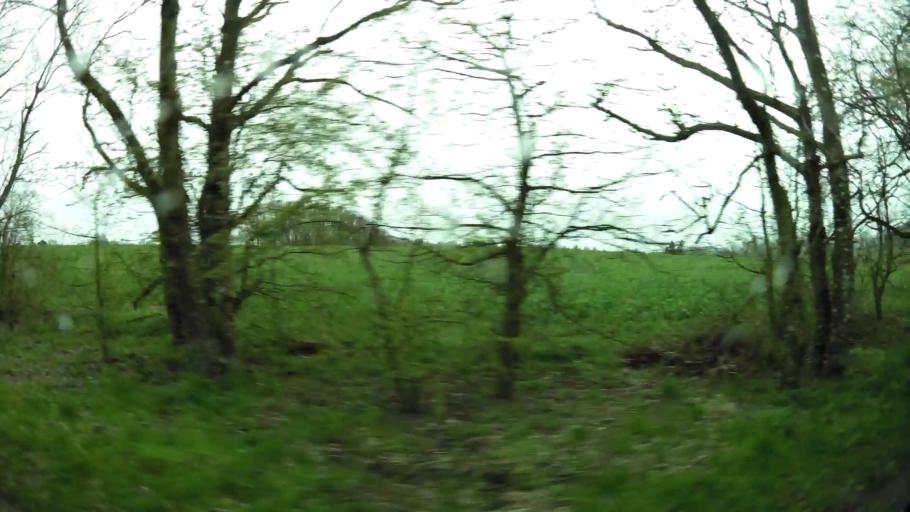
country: DK
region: Central Jutland
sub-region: Holstebro Kommune
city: Vinderup
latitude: 56.4060
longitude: 8.7669
